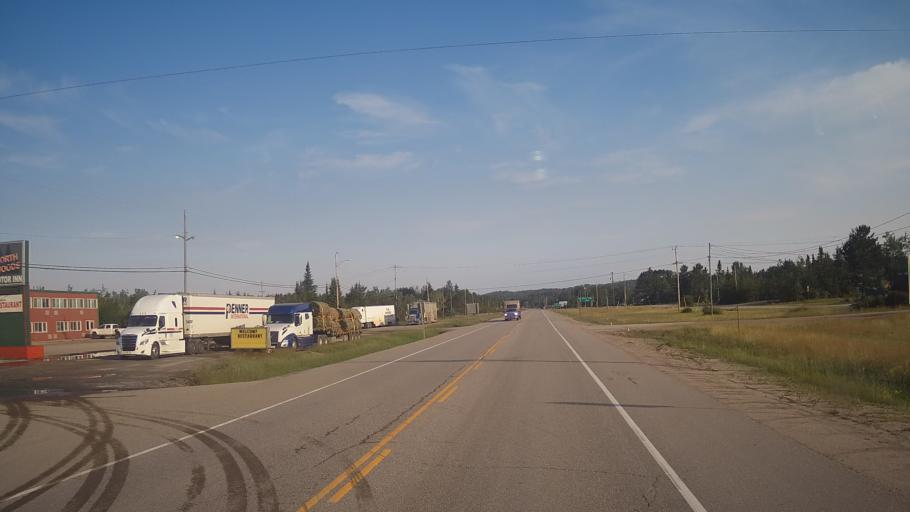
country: CA
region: Ontario
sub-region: Rainy River District
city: Atikokan
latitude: 49.4090
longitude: -91.6413
